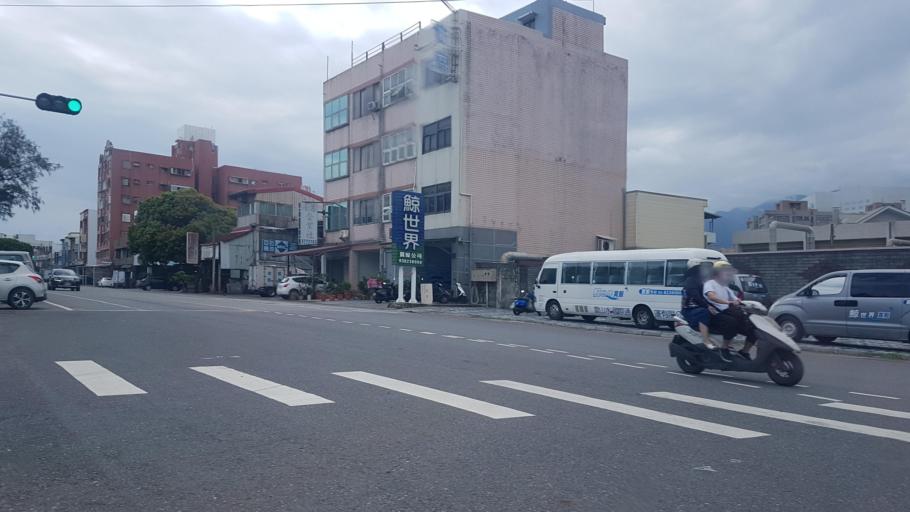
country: TW
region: Taiwan
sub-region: Hualien
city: Hualian
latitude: 23.9995
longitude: 121.6327
